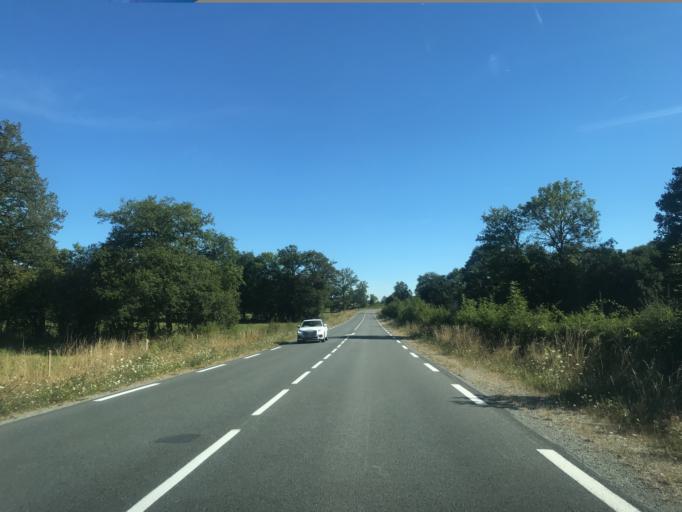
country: FR
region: Limousin
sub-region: Departement de la Creuse
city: Gouzon
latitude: 46.1607
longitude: 2.2118
